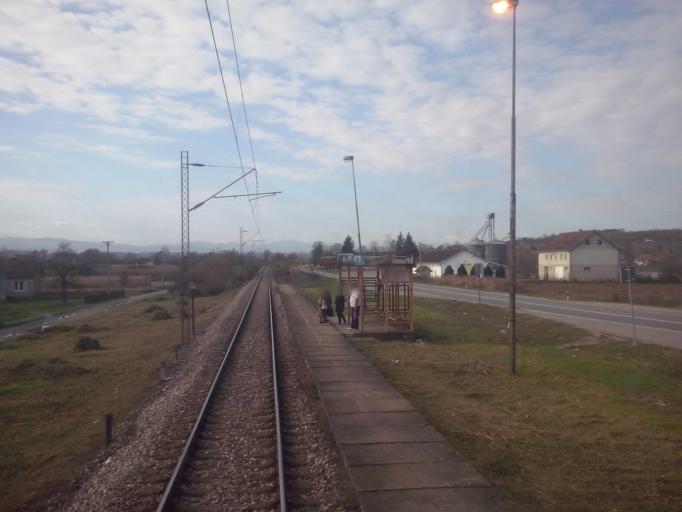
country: RS
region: Central Serbia
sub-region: Kolubarski Okrug
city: Mionica
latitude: 44.3125
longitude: 20.0633
